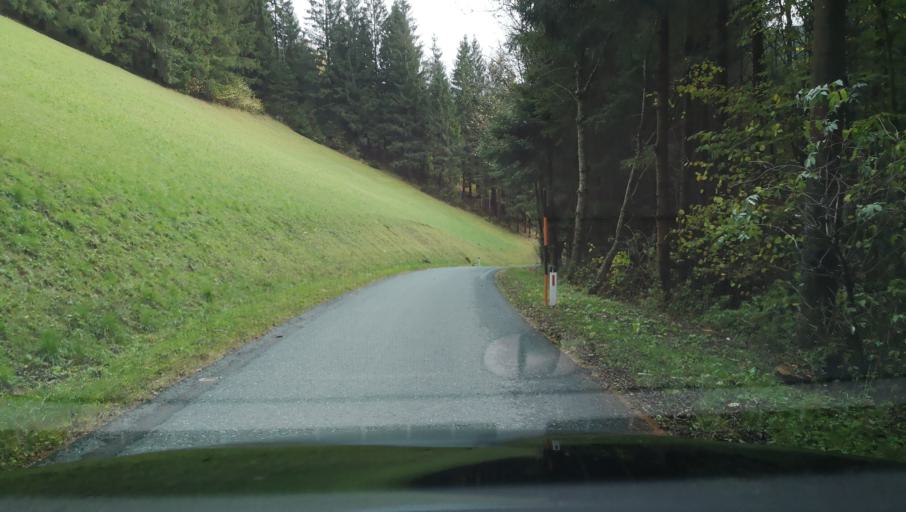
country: AT
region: Styria
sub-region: Politischer Bezirk Weiz
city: Birkfeld
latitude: 47.3700
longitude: 15.6300
